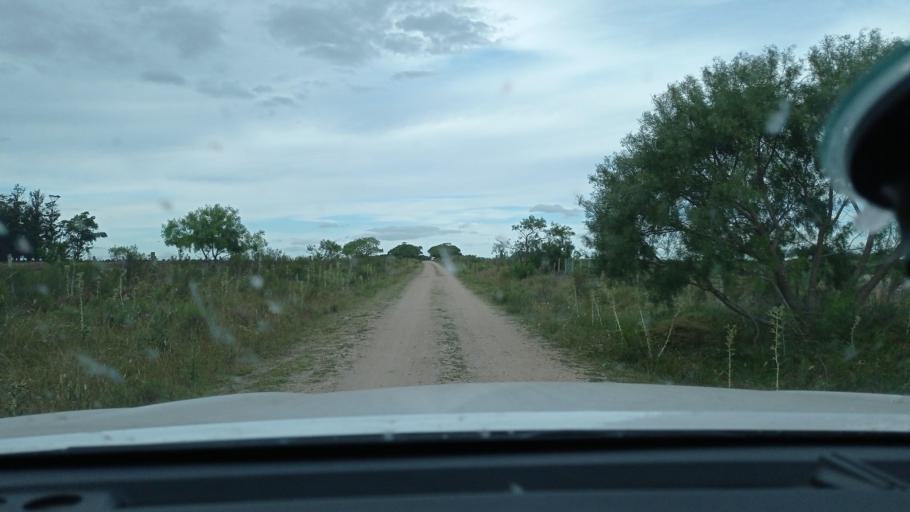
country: UY
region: Florida
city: Casupa
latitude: -34.1183
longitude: -55.8206
